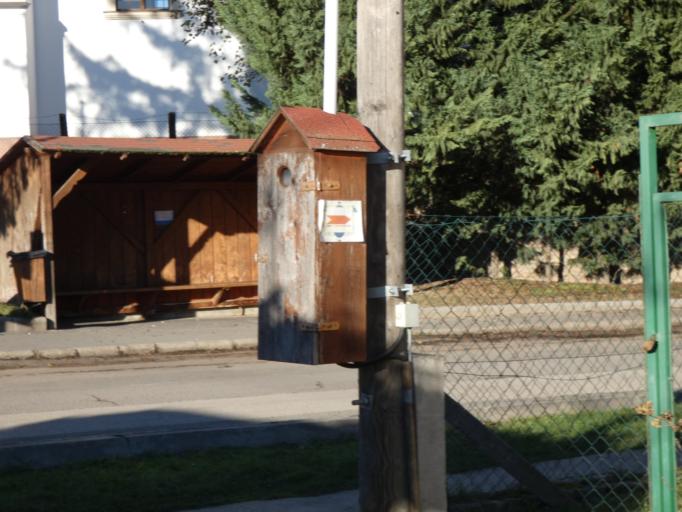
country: HU
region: Pest
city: Gomba
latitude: 47.3705
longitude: 19.5313
